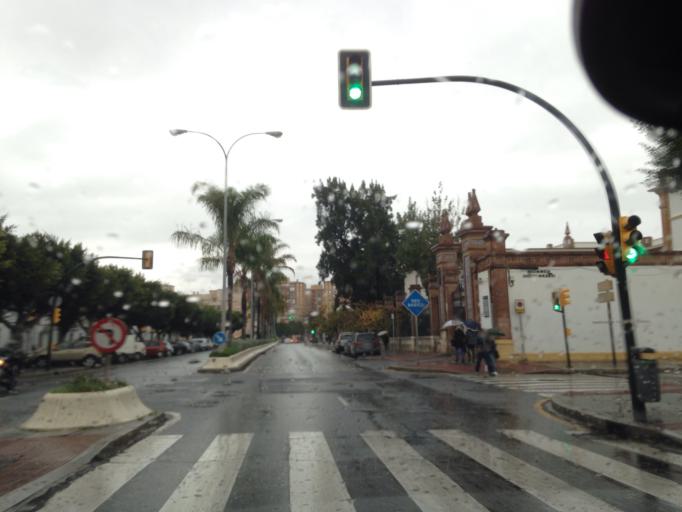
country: ES
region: Andalusia
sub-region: Provincia de Malaga
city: Malaga
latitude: 36.6983
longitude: -4.4408
